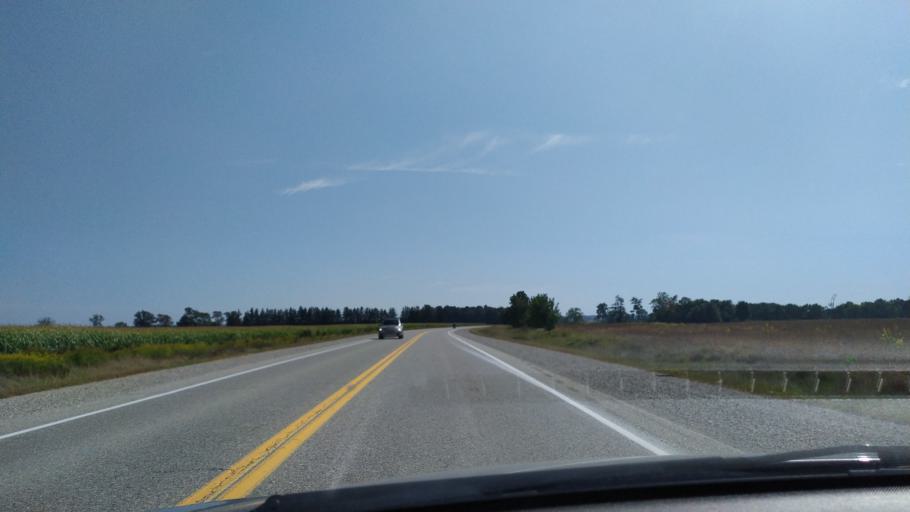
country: CA
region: Ontario
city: Ingersoll
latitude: 43.0905
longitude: -80.8677
